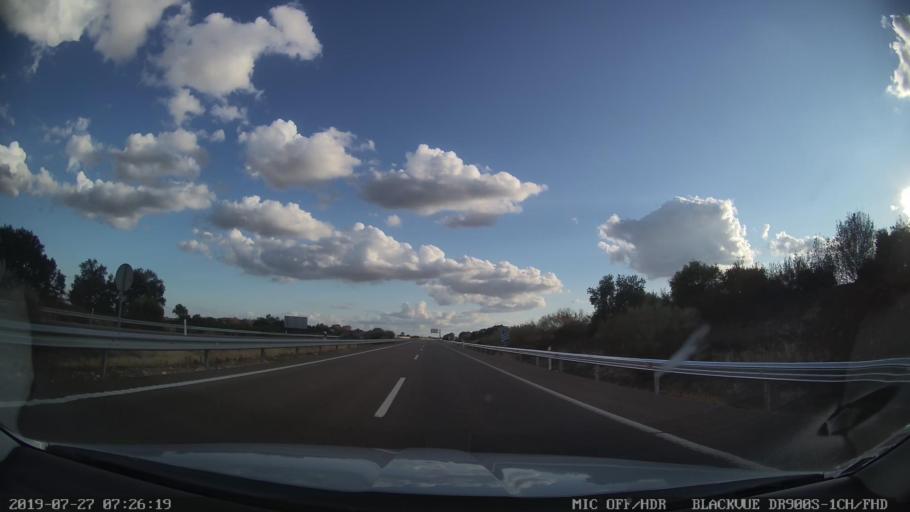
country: ES
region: Extremadura
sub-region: Provincia de Caceres
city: Villamesias
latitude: 39.2607
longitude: -5.8619
